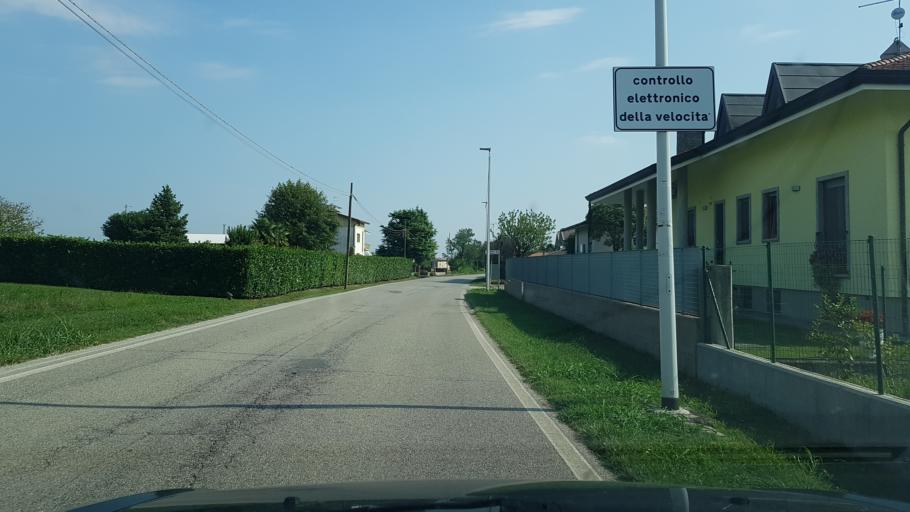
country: IT
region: Friuli Venezia Giulia
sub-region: Provincia di Udine
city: San Vito di Fagagna
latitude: 46.0728
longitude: 13.0788
